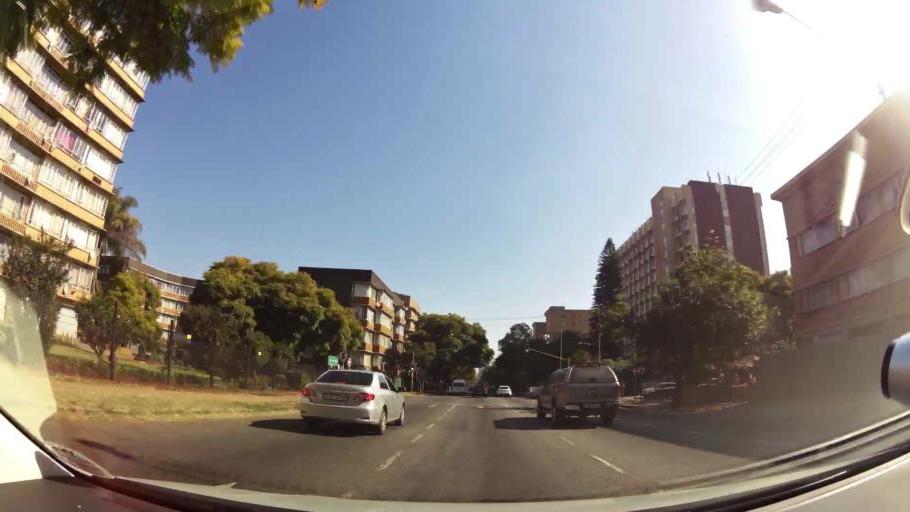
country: ZA
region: Gauteng
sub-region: City of Tshwane Metropolitan Municipality
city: Pretoria
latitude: -25.7463
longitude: 28.2126
